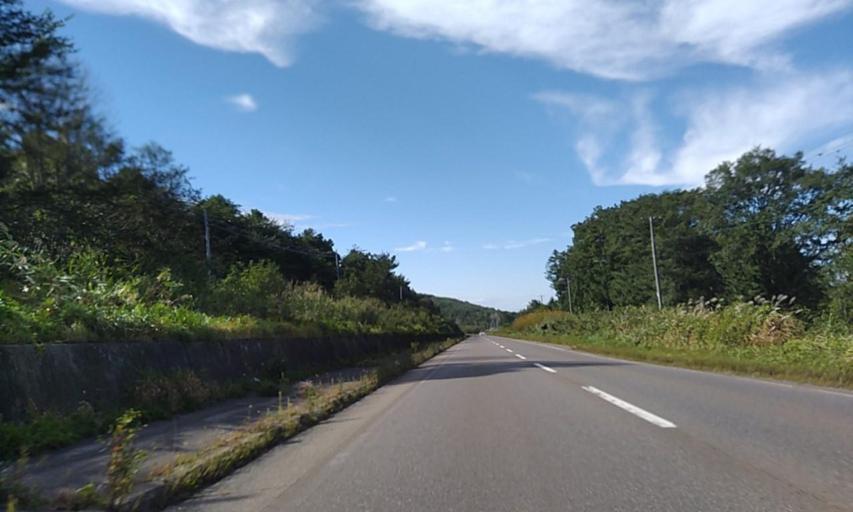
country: JP
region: Hokkaido
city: Obihiro
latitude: 42.8256
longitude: 143.4741
